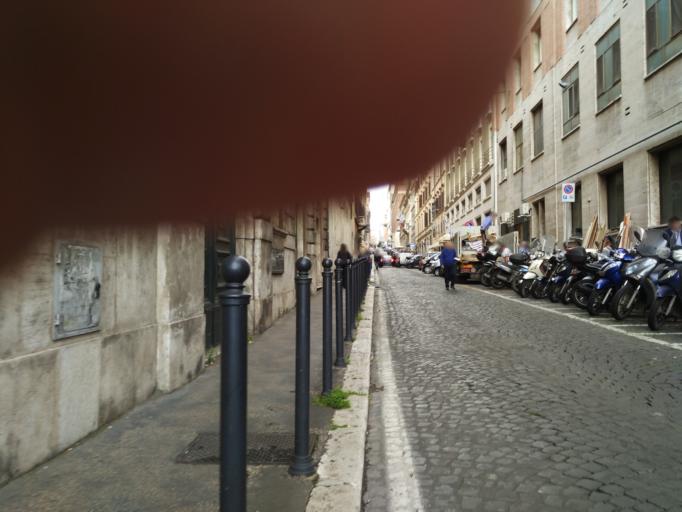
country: IT
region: Latium
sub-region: Citta metropolitana di Roma Capitale
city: Rome
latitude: 41.9040
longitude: 12.4891
